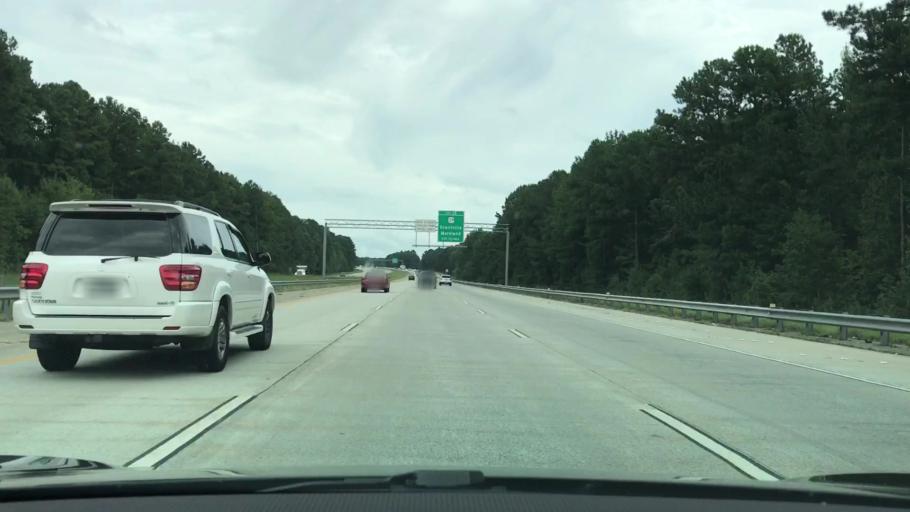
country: US
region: Georgia
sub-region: Coweta County
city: Grantville
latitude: 33.2282
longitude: -84.8102
